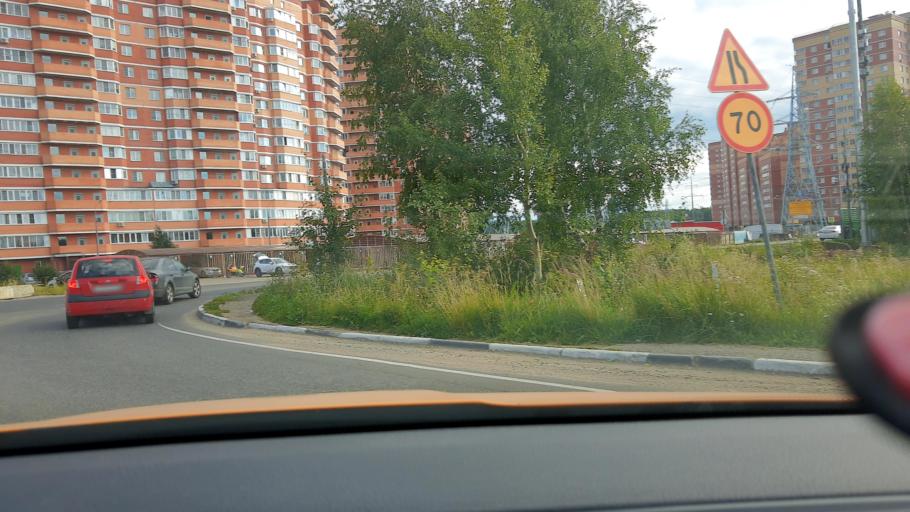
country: RU
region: Moskovskaya
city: Zvenigorod
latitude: 55.7464
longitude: 36.8804
